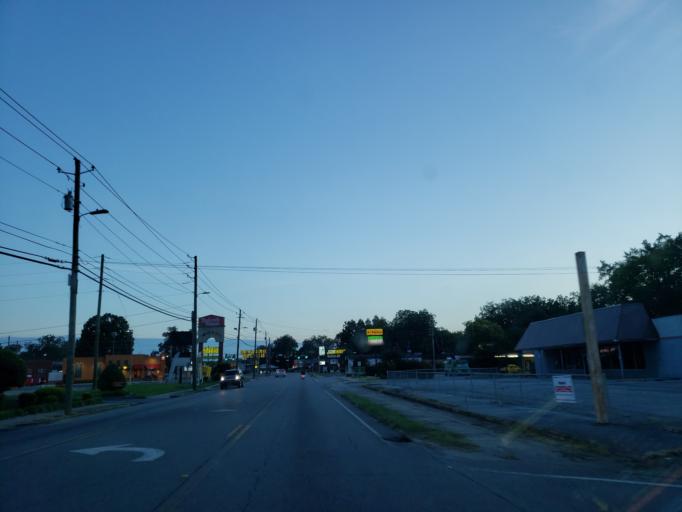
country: US
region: Georgia
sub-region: Polk County
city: Cedartown
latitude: 34.0190
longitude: -85.2531
